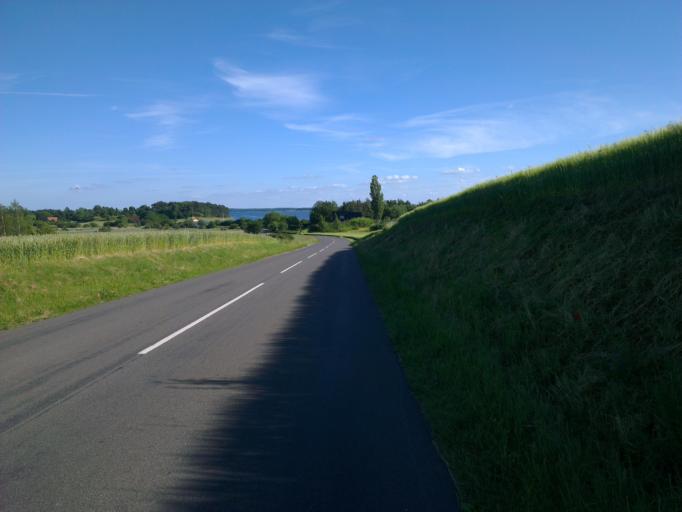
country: DK
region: Capital Region
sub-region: Frederikssund Kommune
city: Skibby
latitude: 55.7455
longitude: 11.9866
